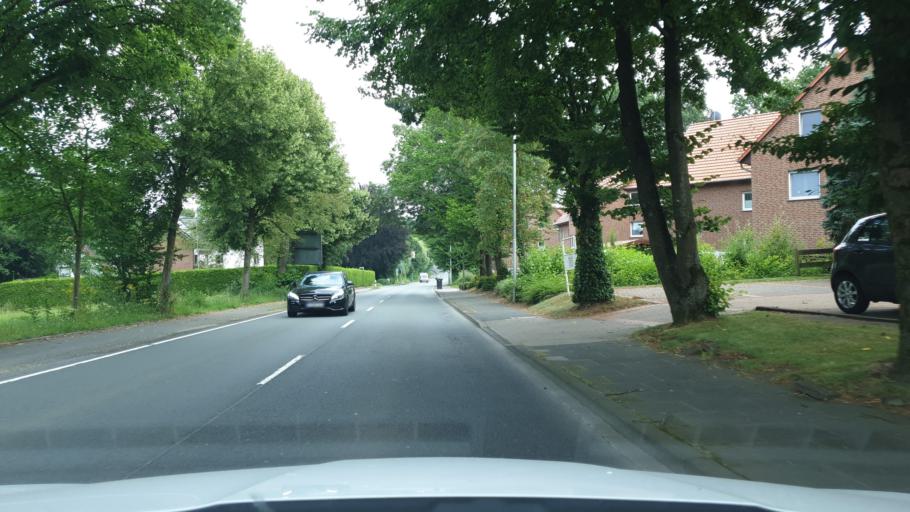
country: DE
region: North Rhine-Westphalia
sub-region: Regierungsbezirk Detmold
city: Bad Salzuflen
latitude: 52.1365
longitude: 8.7796
